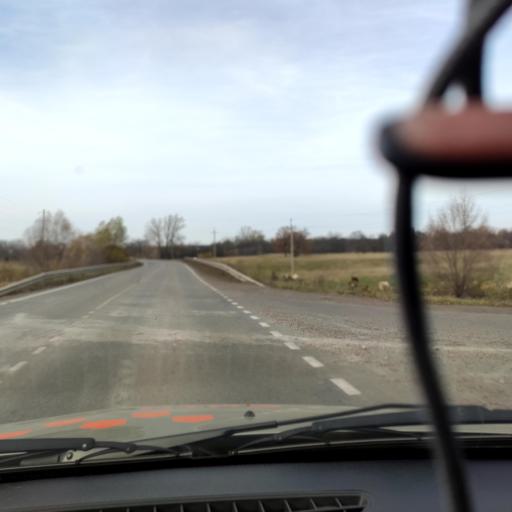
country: RU
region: Bashkortostan
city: Kabakovo
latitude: 54.5624
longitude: 55.9987
